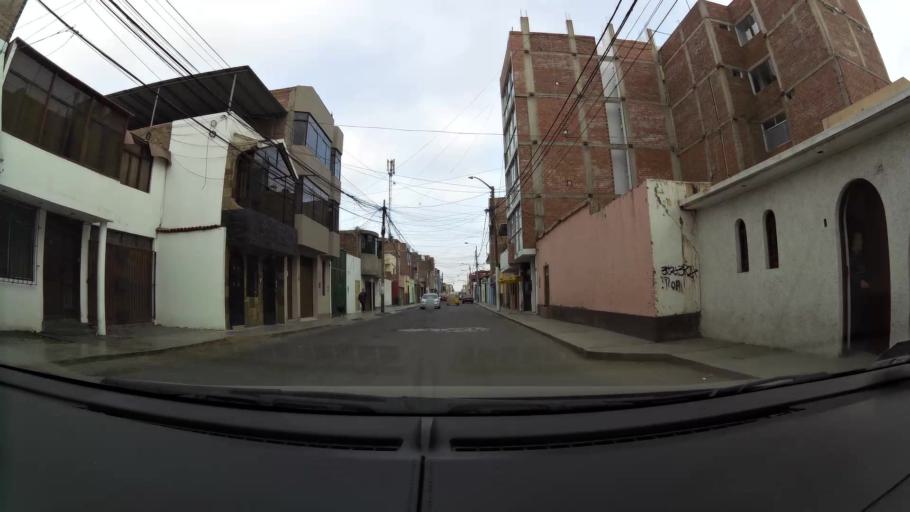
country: PE
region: La Libertad
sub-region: Provincia de Trujillo
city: Trujillo
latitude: -8.1042
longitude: -79.0276
